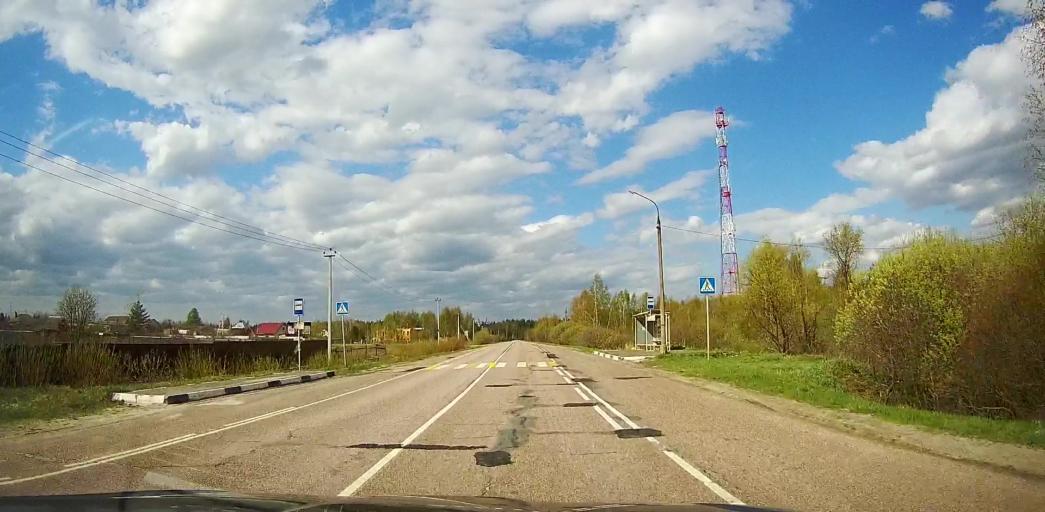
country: RU
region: Moskovskaya
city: Rakhmanovo
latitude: 55.6552
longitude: 38.6390
